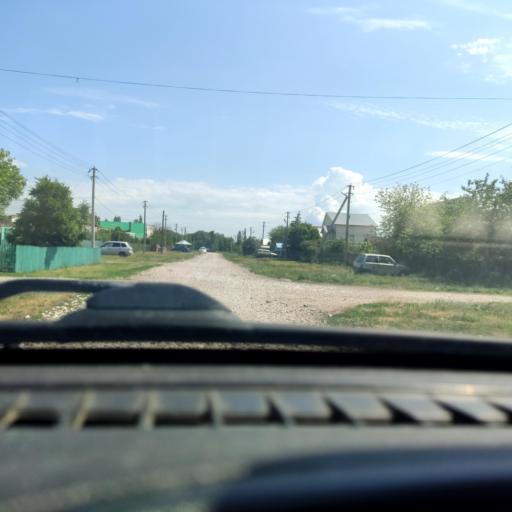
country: RU
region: Samara
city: Tol'yatti
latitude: 53.6359
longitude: 49.2944
